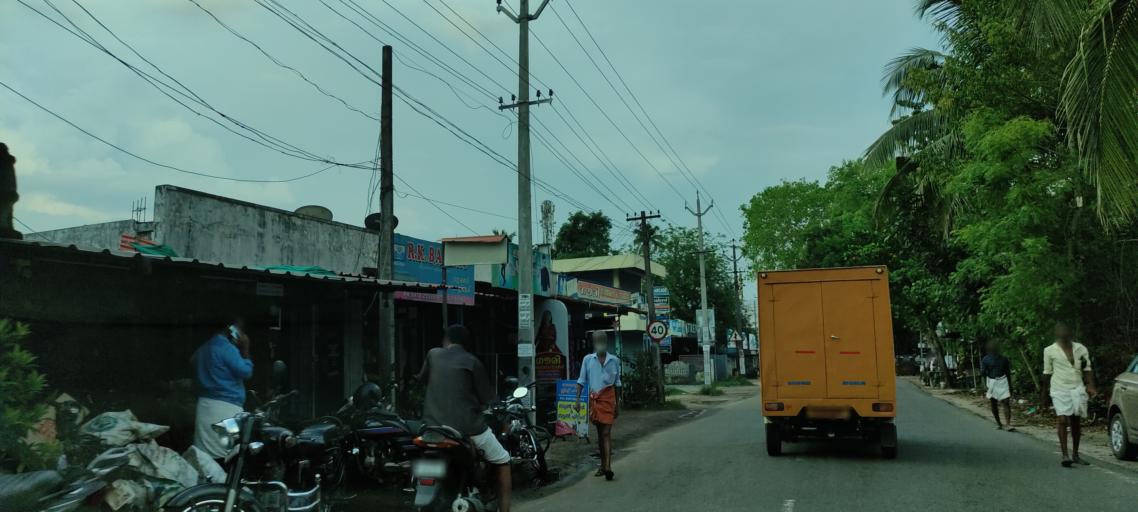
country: IN
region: Kerala
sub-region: Kottayam
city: Vaikam
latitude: 9.7562
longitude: 76.3629
